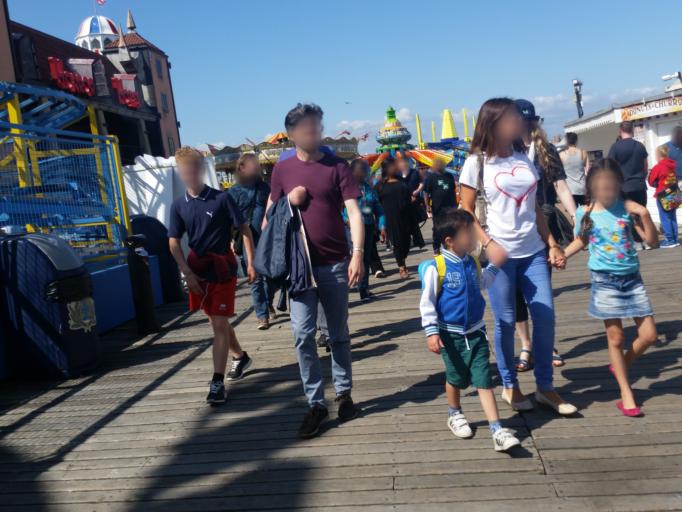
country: GB
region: England
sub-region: Brighton and Hove
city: Brighton
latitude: 50.8151
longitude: -0.1373
